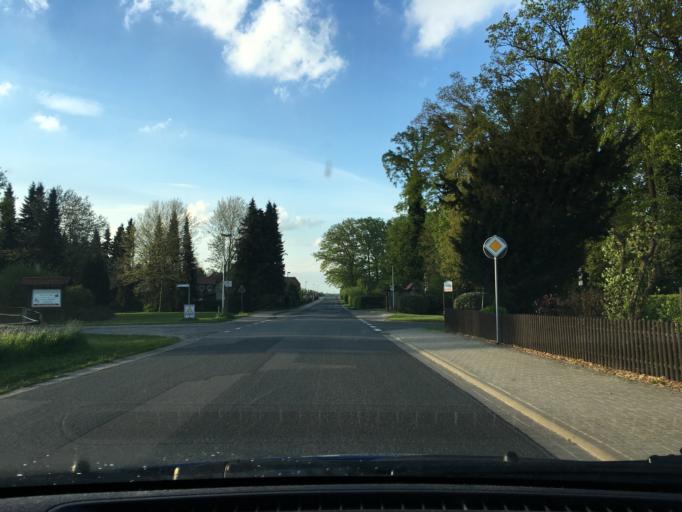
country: DE
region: Lower Saxony
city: Bergen
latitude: 52.8256
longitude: 9.9710
